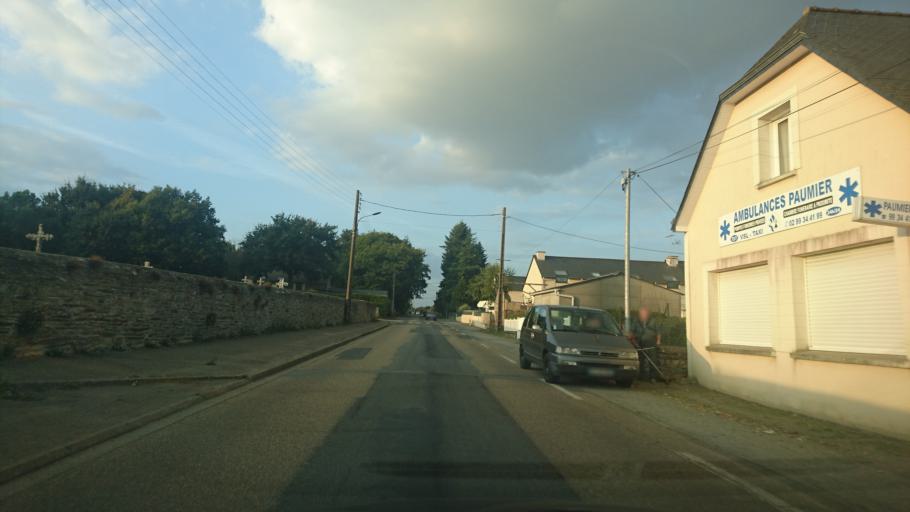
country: FR
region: Brittany
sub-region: Departement d'Ille-et-Vilaine
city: Pipriac
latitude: 47.8112
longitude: -1.9467
